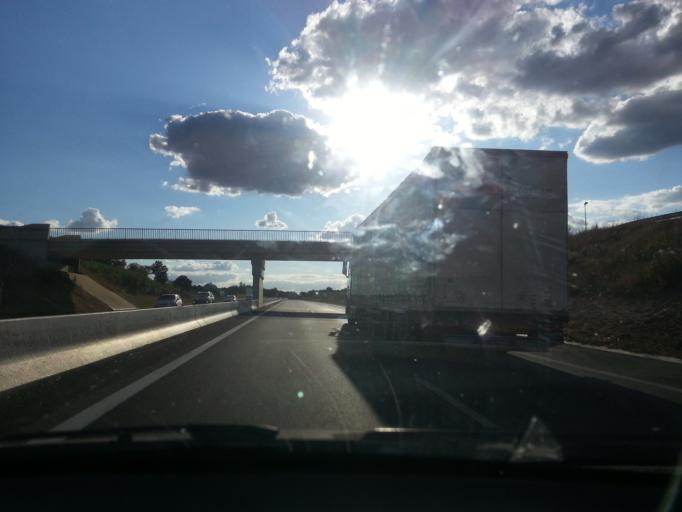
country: FR
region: Bourgogne
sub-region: Departement de Saone-et-Loire
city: Saint-Remy
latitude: 46.7555
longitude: 4.8167
